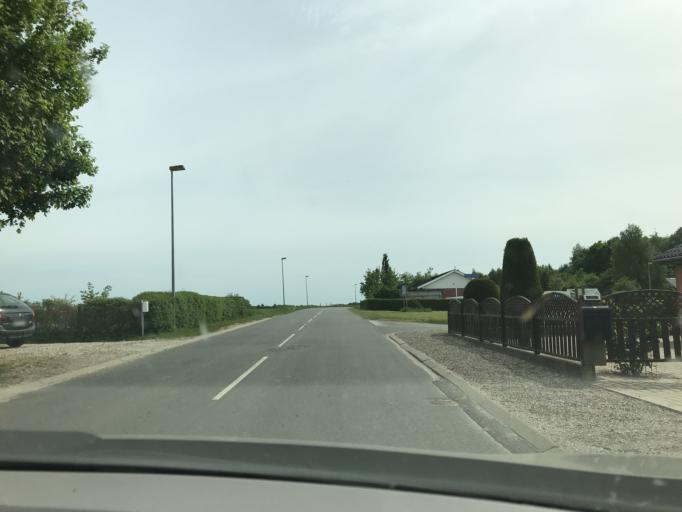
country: DK
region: Central Jutland
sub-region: Norddjurs Kommune
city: Allingabro
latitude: 56.5488
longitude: 10.2999
